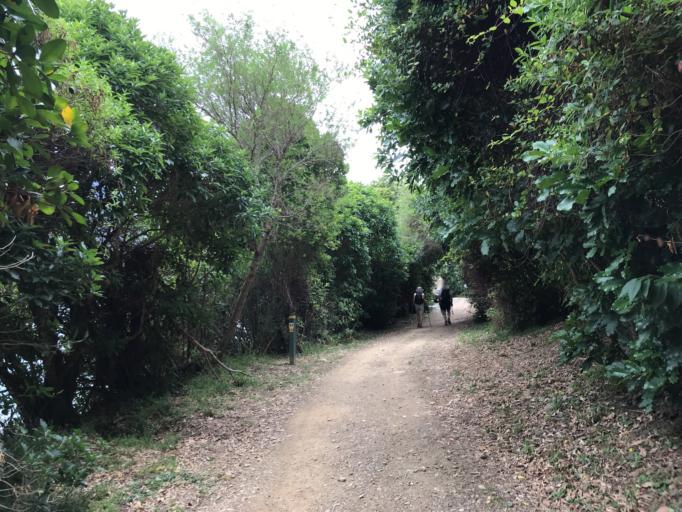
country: NZ
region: Marlborough
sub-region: Marlborough District
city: Picton
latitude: -41.1012
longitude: 174.1843
